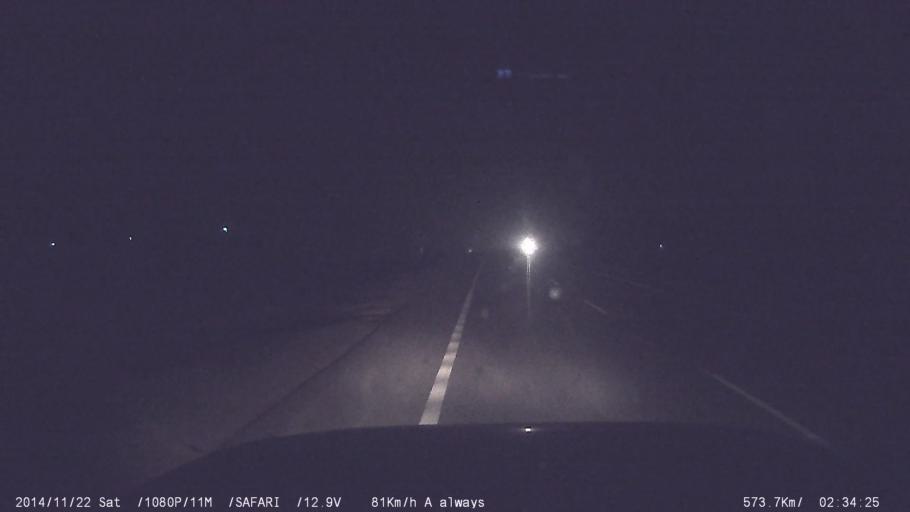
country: IN
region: Tamil Nadu
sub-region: Salem
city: Belur
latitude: 11.6491
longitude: 78.3993
